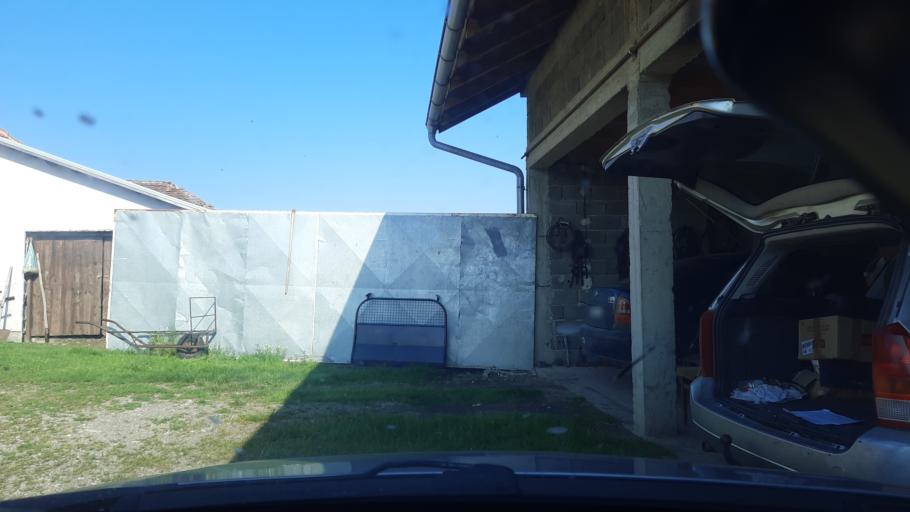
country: RS
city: Prislonica
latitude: 43.9133
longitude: 20.4289
